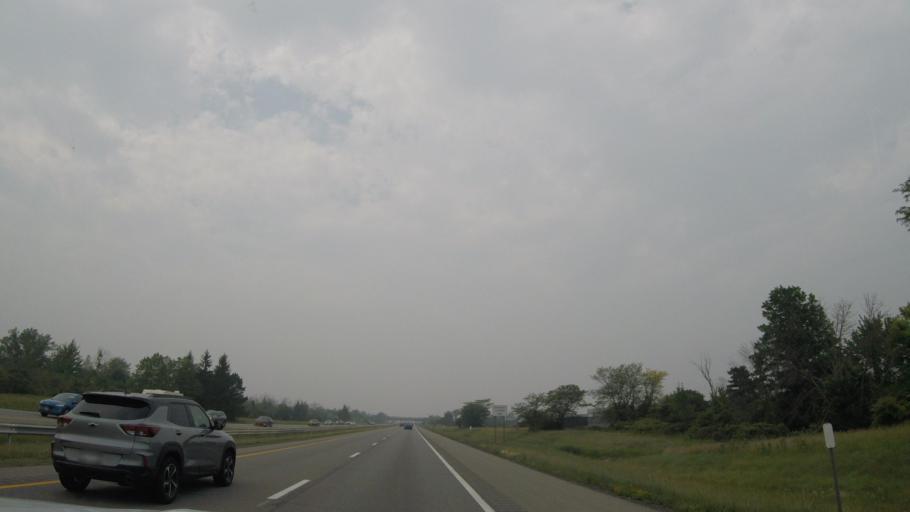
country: US
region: New York
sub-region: Erie County
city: Grandyle Village
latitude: 43.0311
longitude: -78.9807
